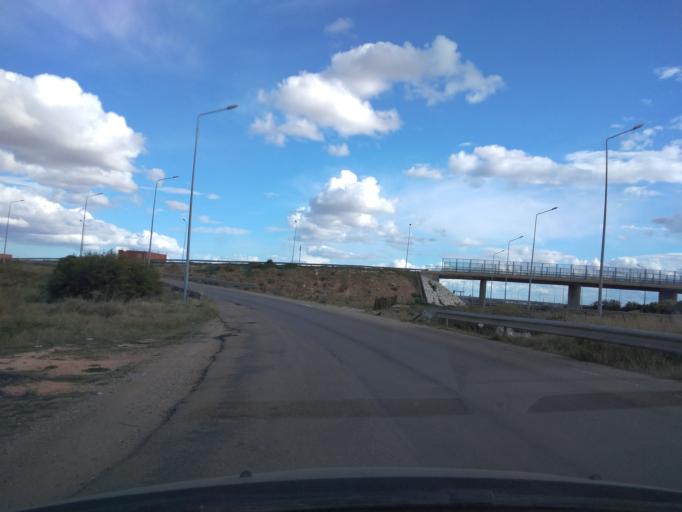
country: TN
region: Susah
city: Masakin
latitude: 35.7130
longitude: 10.5578
